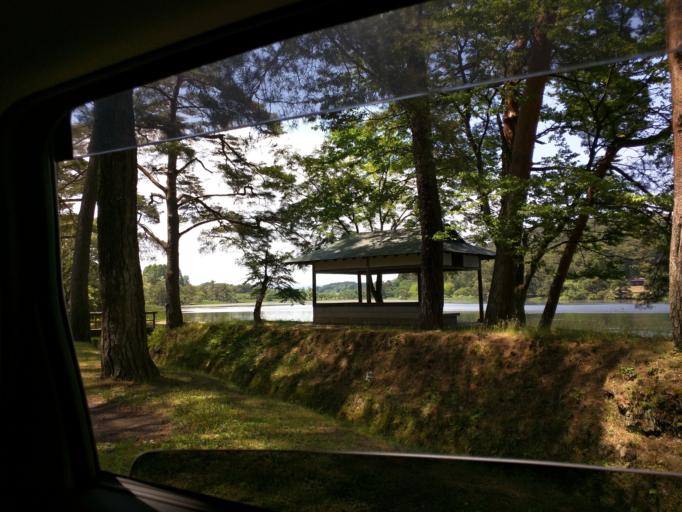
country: JP
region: Tochigi
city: Kuroiso
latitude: 37.1075
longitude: 140.2175
